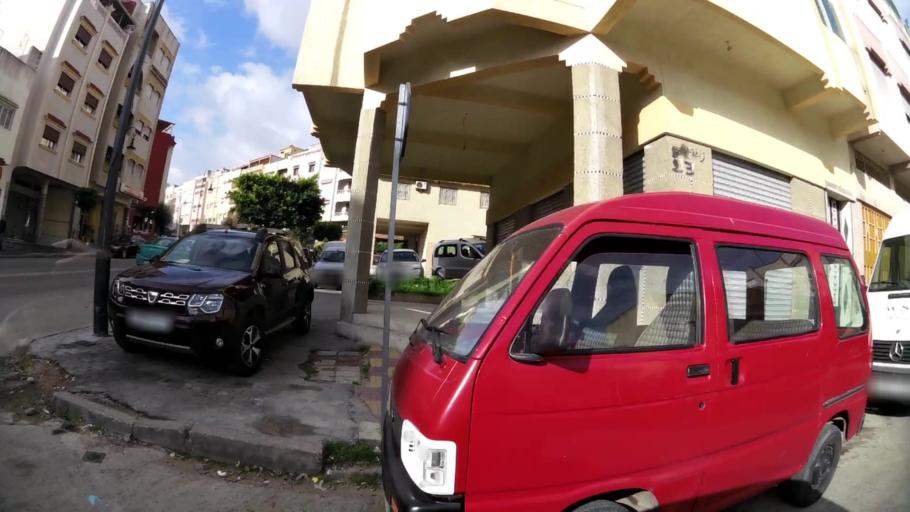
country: MA
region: Tanger-Tetouan
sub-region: Tanger-Assilah
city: Tangier
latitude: 35.7631
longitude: -5.8316
